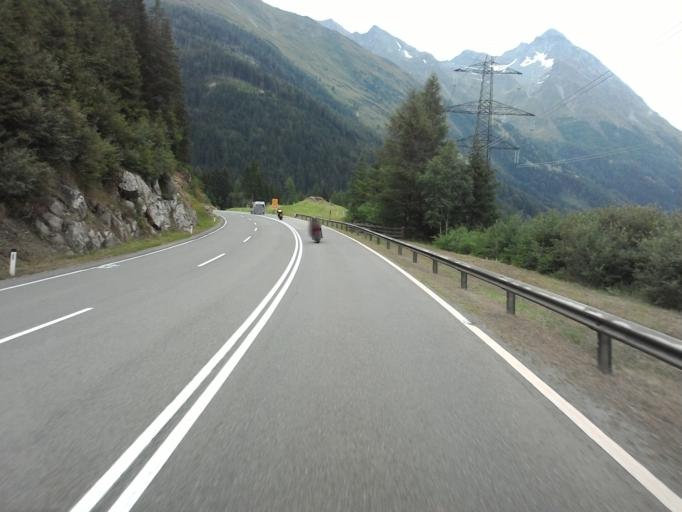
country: AT
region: Tyrol
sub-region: Politischer Bezirk Lienz
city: Matrei in Osttirol
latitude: 47.0912
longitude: 12.5233
